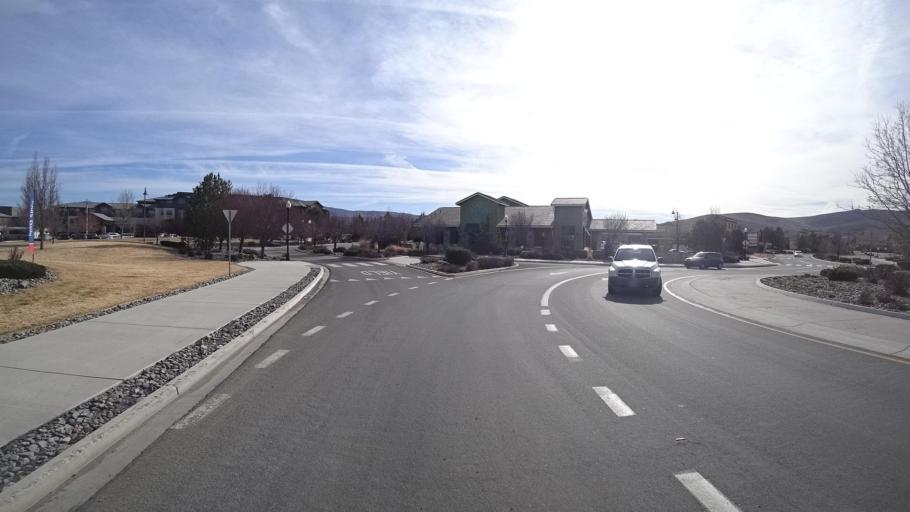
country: US
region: Nevada
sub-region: Washoe County
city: Spanish Springs
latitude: 39.6093
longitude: -119.6978
